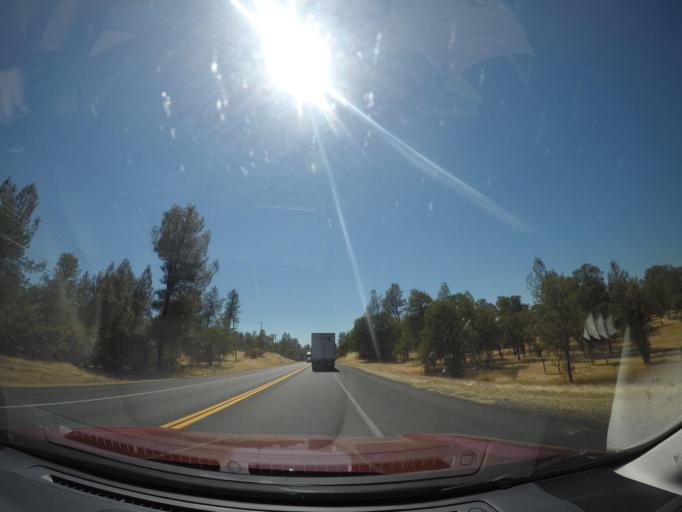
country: US
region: California
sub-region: Shasta County
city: Bella Vista
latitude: 40.6281
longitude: -122.2852
